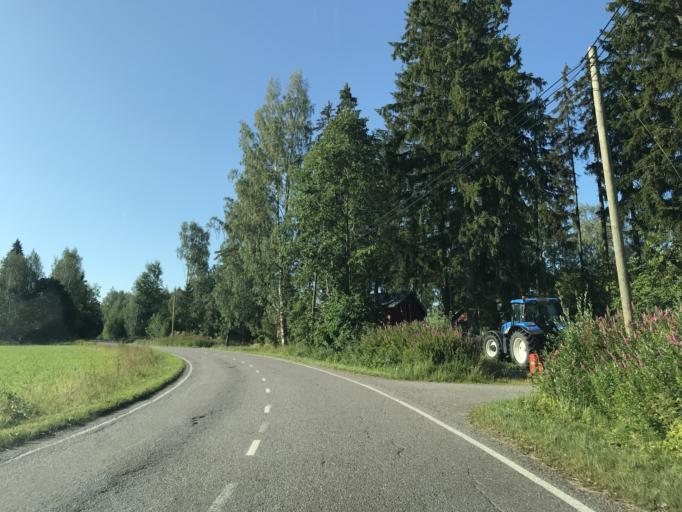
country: FI
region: Uusimaa
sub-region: Helsinki
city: Lohja
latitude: 60.2887
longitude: 24.1377
